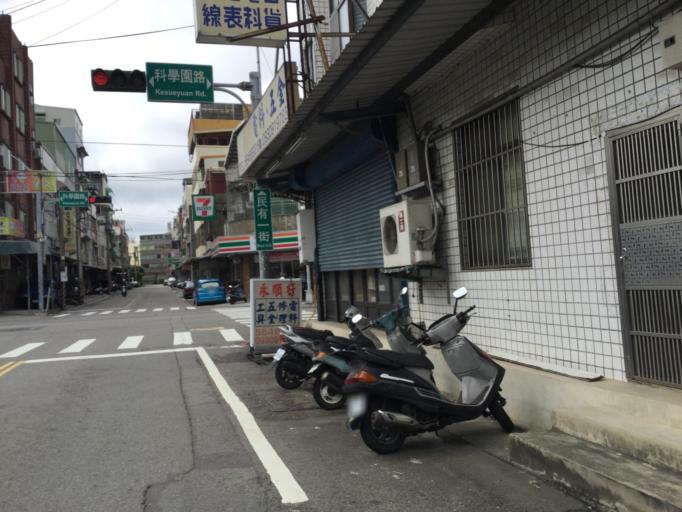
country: TW
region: Taiwan
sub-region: Hsinchu
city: Hsinchu
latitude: 24.7832
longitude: 121.0118
